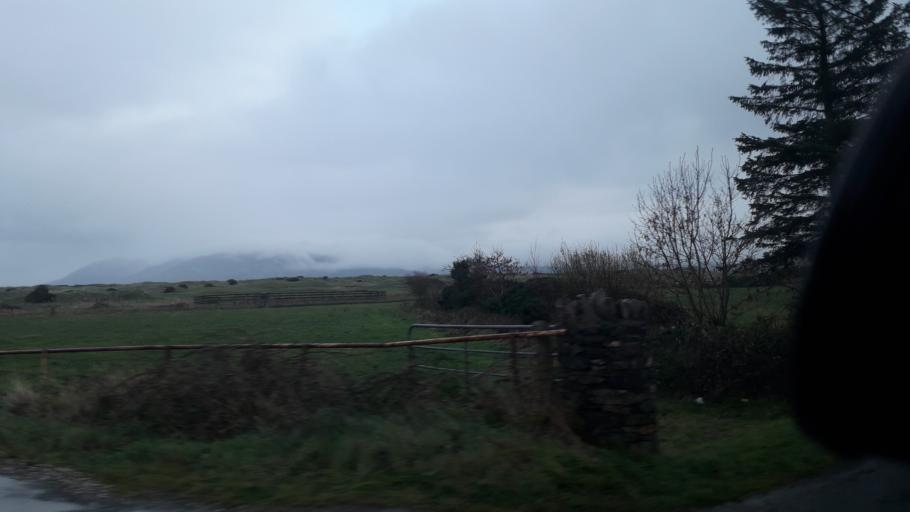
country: IE
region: Ulster
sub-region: County Donegal
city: Ramelton
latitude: 55.1925
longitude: -7.6247
